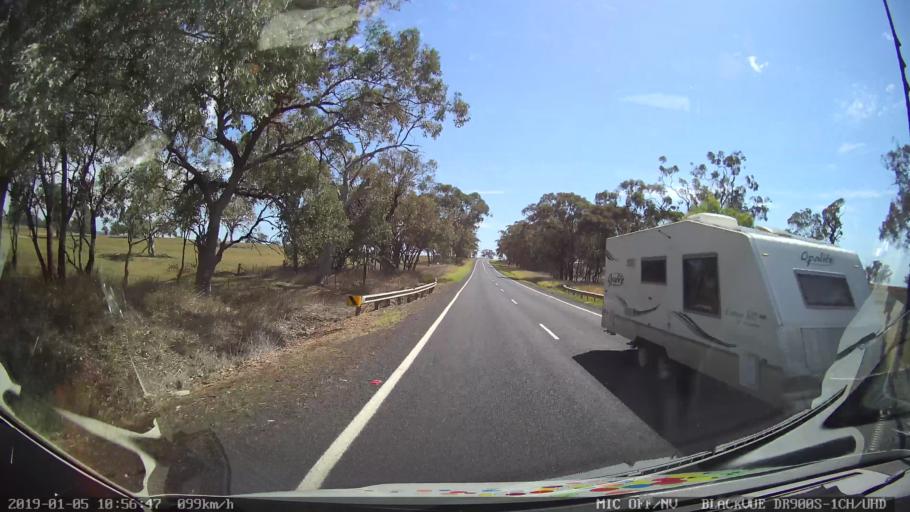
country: AU
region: New South Wales
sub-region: Warrumbungle Shire
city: Coonabarabran
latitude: -31.4377
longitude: 149.1618
